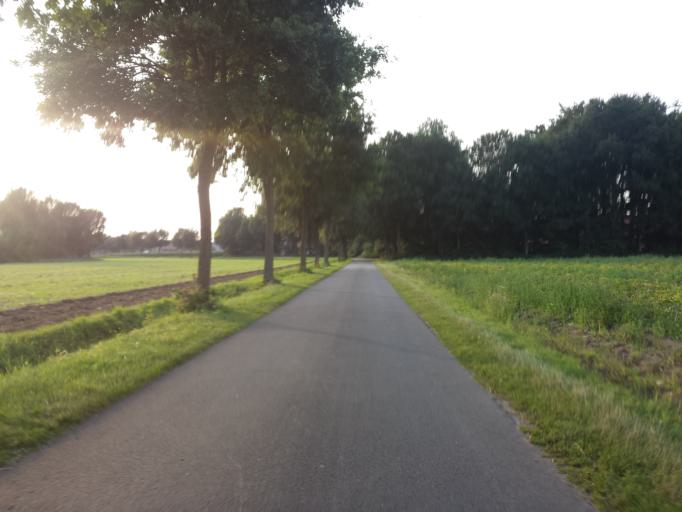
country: DE
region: North Rhine-Westphalia
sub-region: Regierungsbezirk Detmold
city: Guetersloh
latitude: 51.9400
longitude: 8.3133
